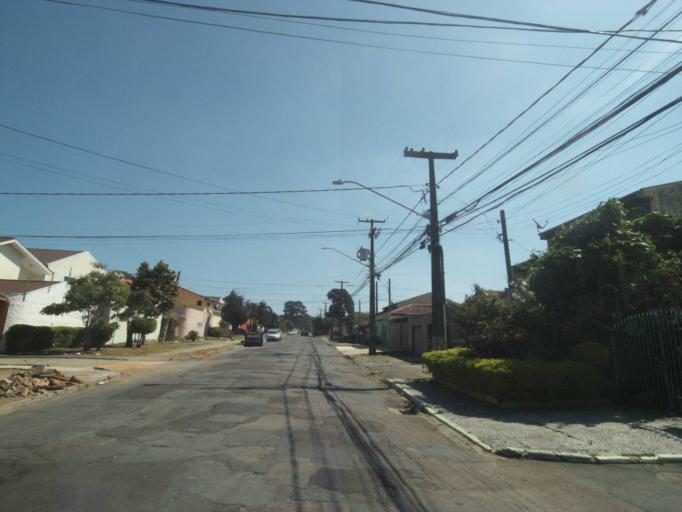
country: BR
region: Parana
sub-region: Sao Jose Dos Pinhais
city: Sao Jose dos Pinhais
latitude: -25.5154
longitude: -49.2399
